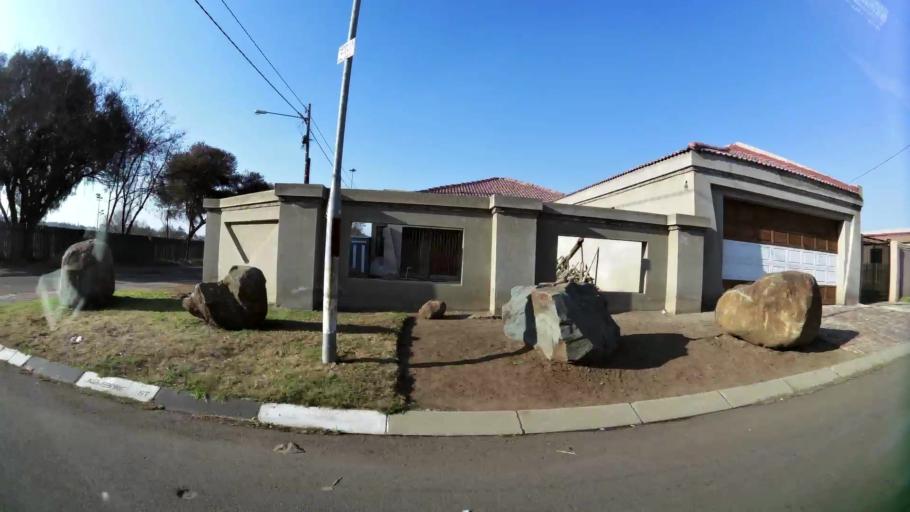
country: ZA
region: Gauteng
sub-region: City of Johannesburg Metropolitan Municipality
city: Soweto
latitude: -26.2636
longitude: 27.8711
